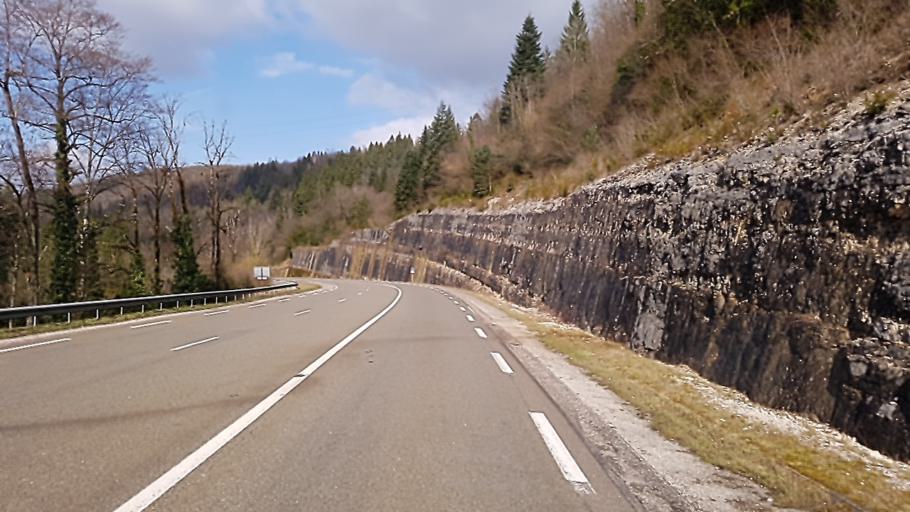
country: FR
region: Rhone-Alpes
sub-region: Departement de l'Ain
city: Dortan
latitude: 46.3373
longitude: 5.6889
